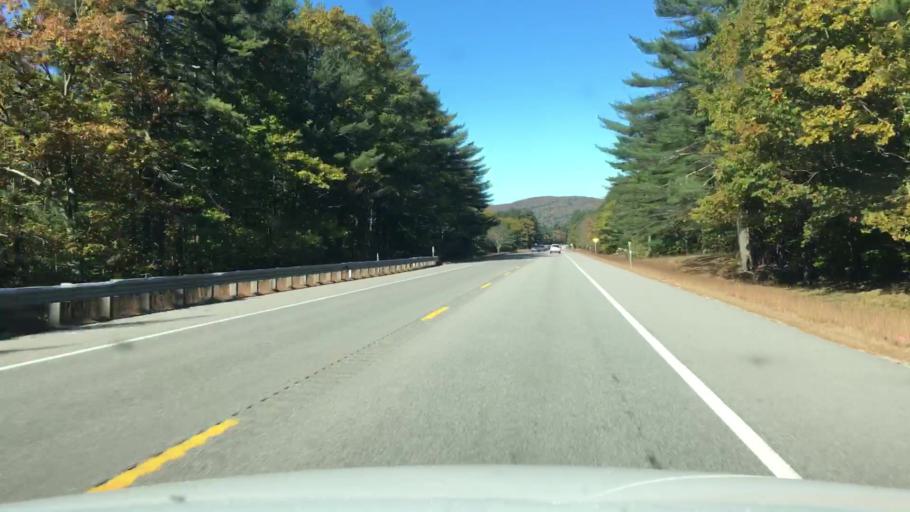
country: US
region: New Hampshire
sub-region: Carroll County
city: Sanbornville
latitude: 43.4916
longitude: -71.0168
